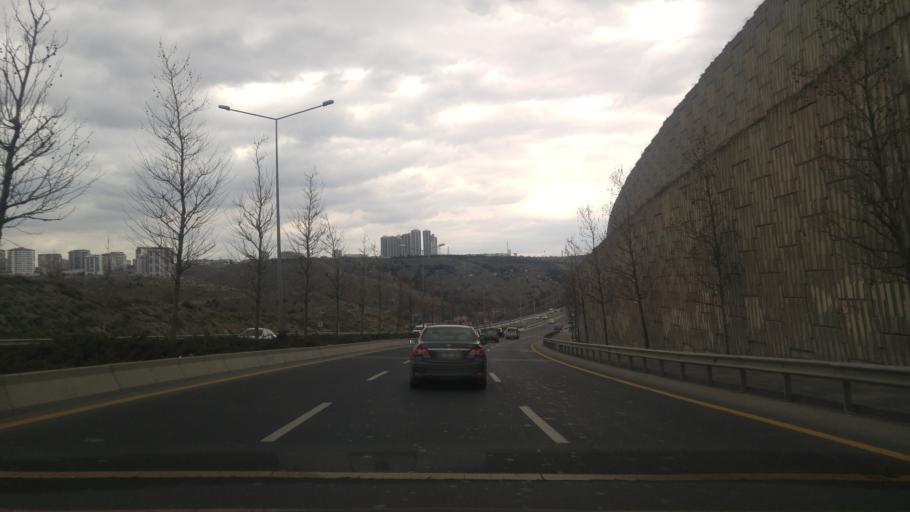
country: TR
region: Ankara
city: Cankaya
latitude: 39.8904
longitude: 32.9017
